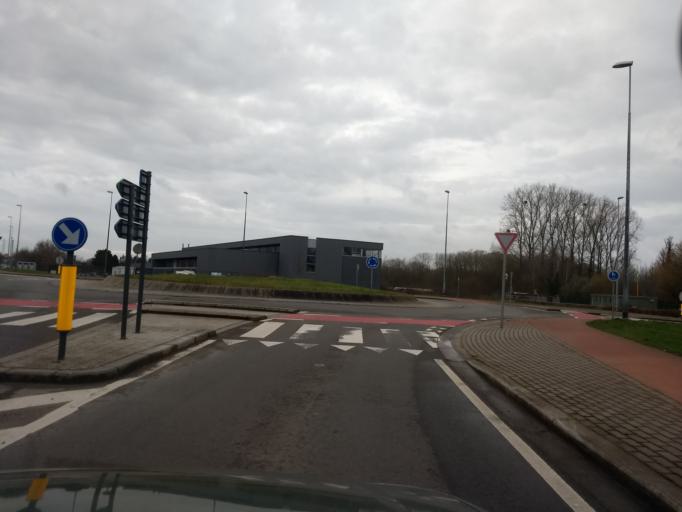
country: BE
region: Flanders
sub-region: Provincie Vlaams-Brabant
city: Liedekerke
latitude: 50.8620
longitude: 4.0811
